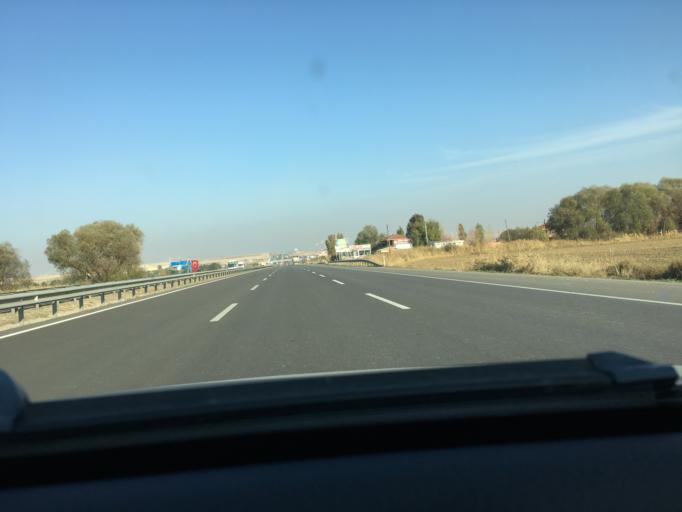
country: TR
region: Ankara
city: Temelli
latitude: 39.7319
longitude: 32.3774
